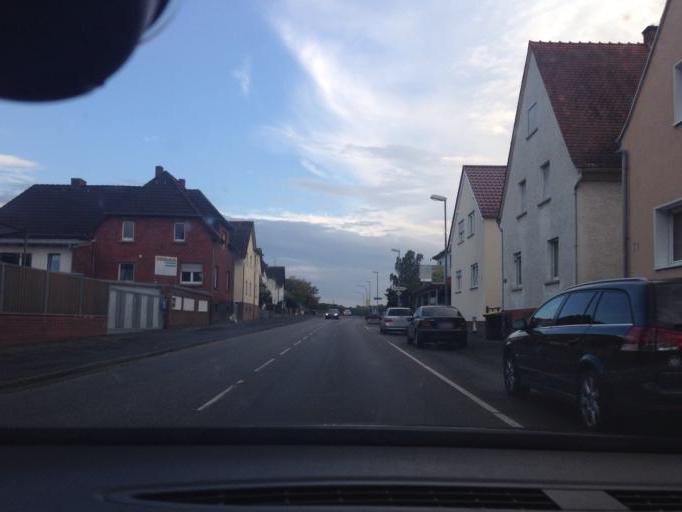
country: DE
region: Hesse
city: Lollar
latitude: 50.6429
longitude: 8.7042
